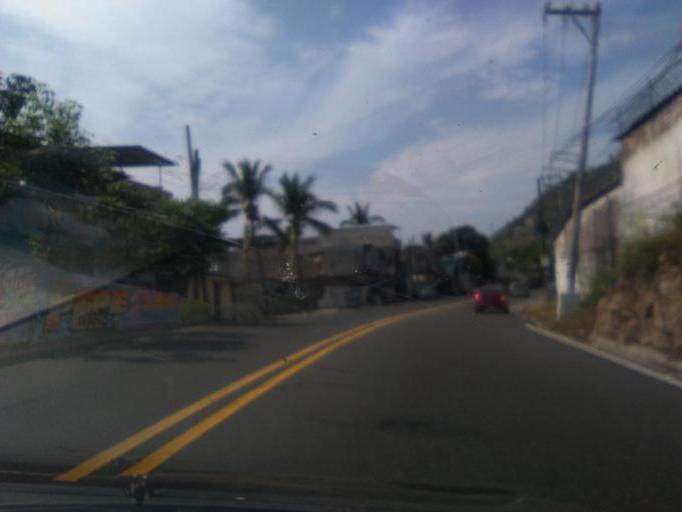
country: MX
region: Guerrero
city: Acapulco de Juarez
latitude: 16.8617
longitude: -99.9251
